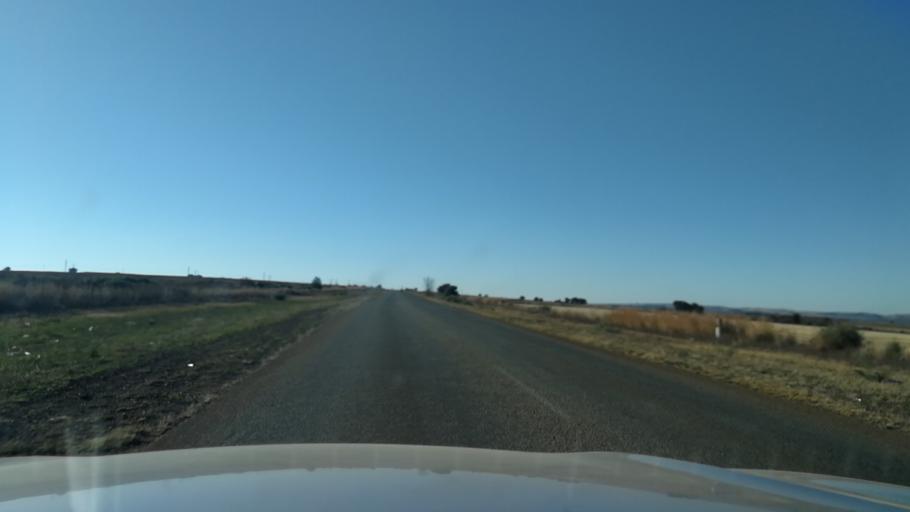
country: ZA
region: North-West
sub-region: Bojanala Platinum District Municipality
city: Rustenburg
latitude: -25.9864
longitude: 27.2768
